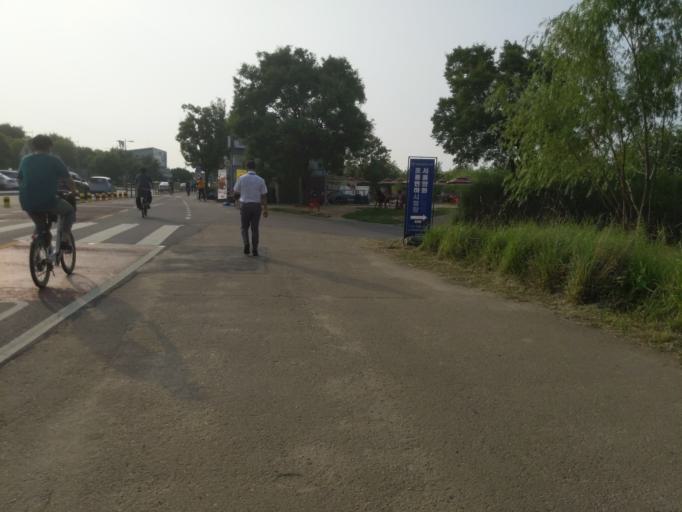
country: KR
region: Gyeonggi-do
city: Kwangmyong
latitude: 37.5373
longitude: 126.9043
